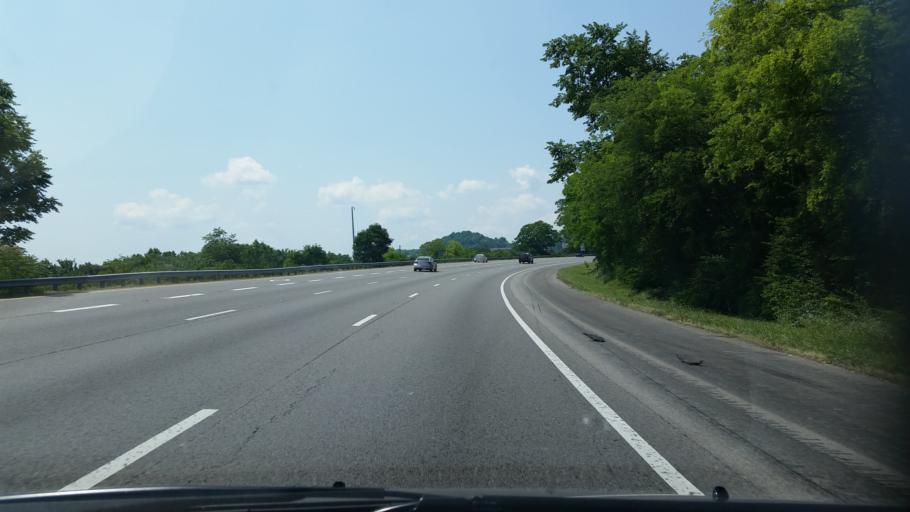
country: US
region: Tennessee
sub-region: Williamson County
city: Brentwood
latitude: 36.0499
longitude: -86.7757
